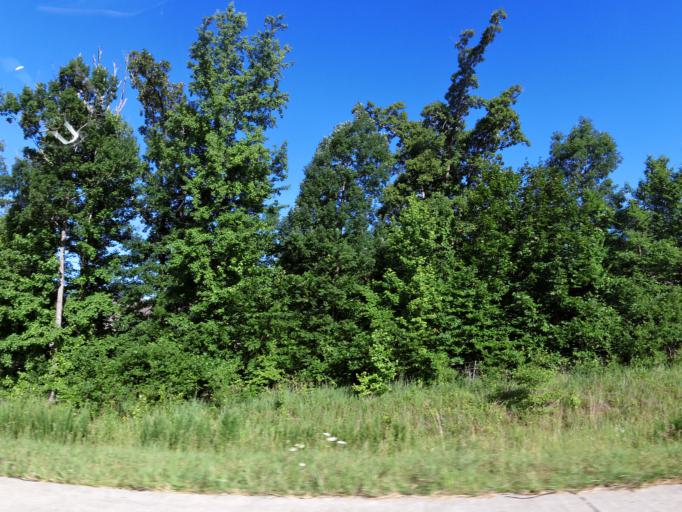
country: US
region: Missouri
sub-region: Butler County
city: Poplar Bluff
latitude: 36.7768
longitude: -90.4552
